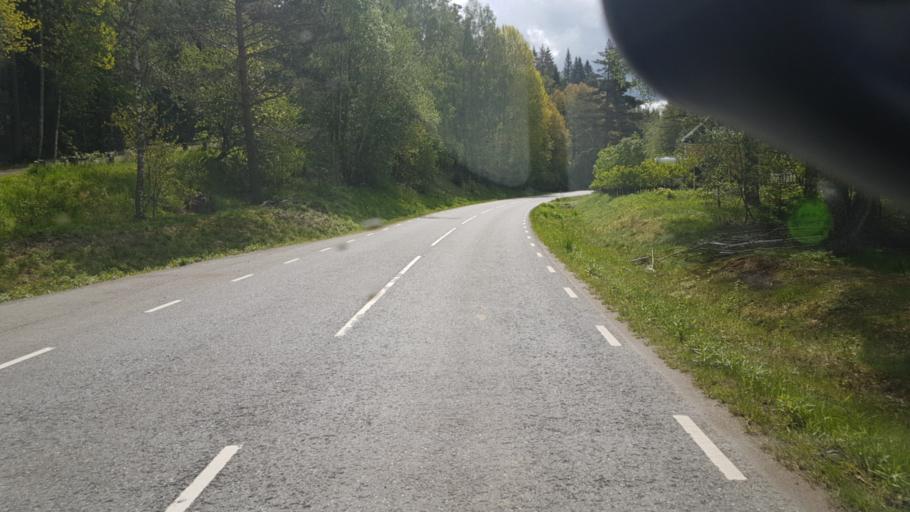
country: NO
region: Ostfold
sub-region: Romskog
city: Romskog
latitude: 59.6970
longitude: 12.0889
